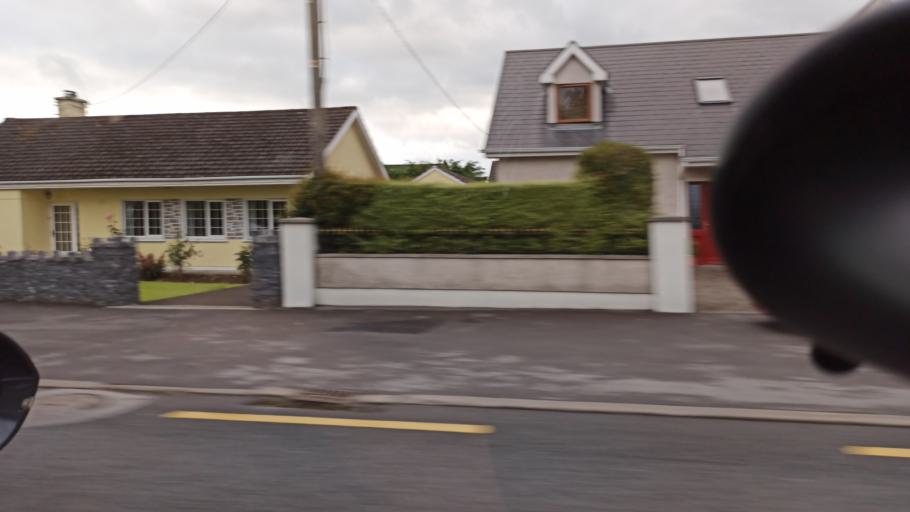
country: IE
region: Munster
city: Thurles
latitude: 52.6900
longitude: -7.8120
